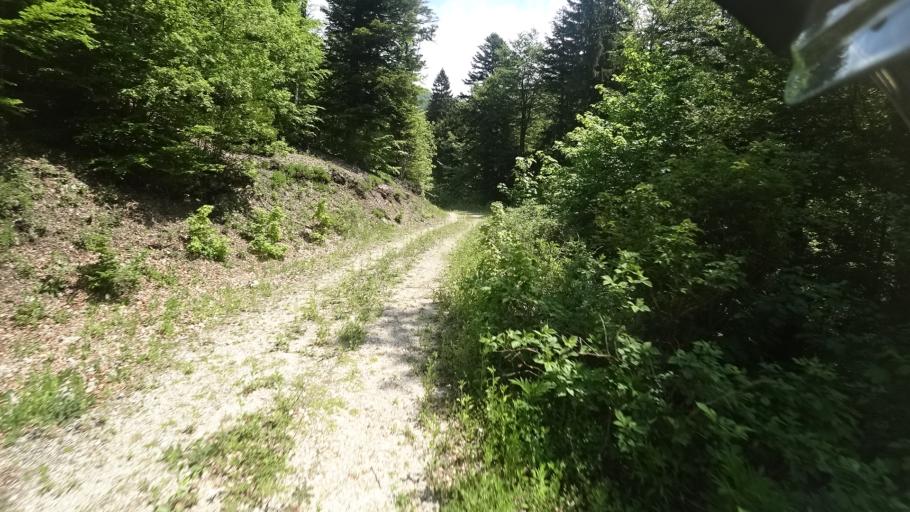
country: BA
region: Federation of Bosnia and Herzegovina
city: Orasac
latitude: 44.5642
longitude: 15.8601
